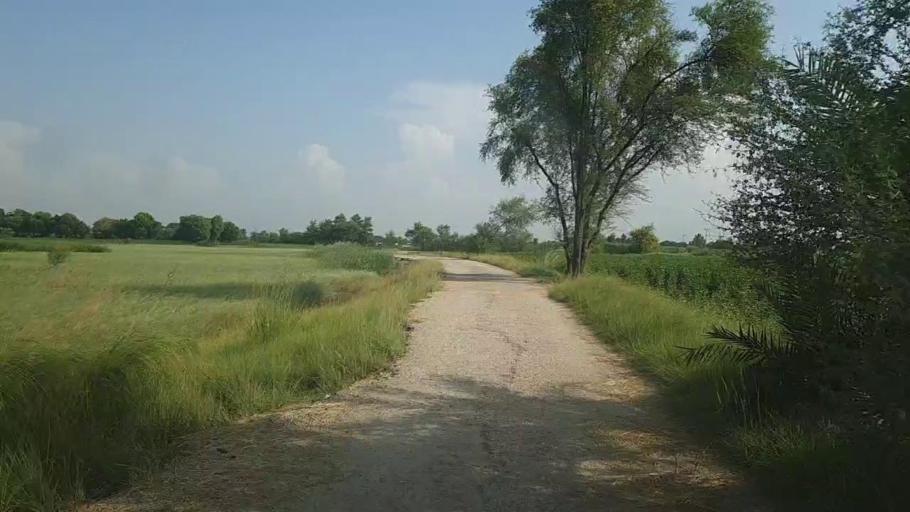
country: PK
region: Sindh
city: Ubauro
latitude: 28.1710
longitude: 69.7737
